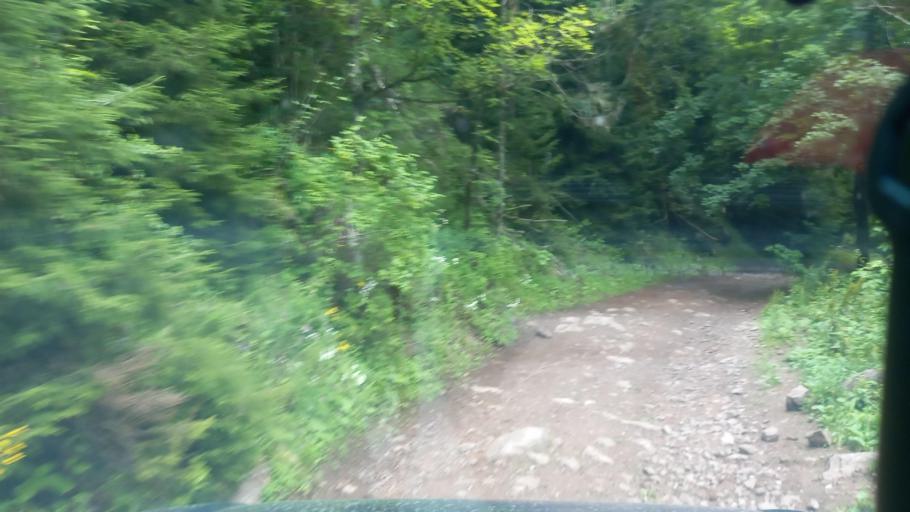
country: RU
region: Karachayevo-Cherkesiya
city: Kurdzhinovo
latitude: 43.8146
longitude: 40.8774
